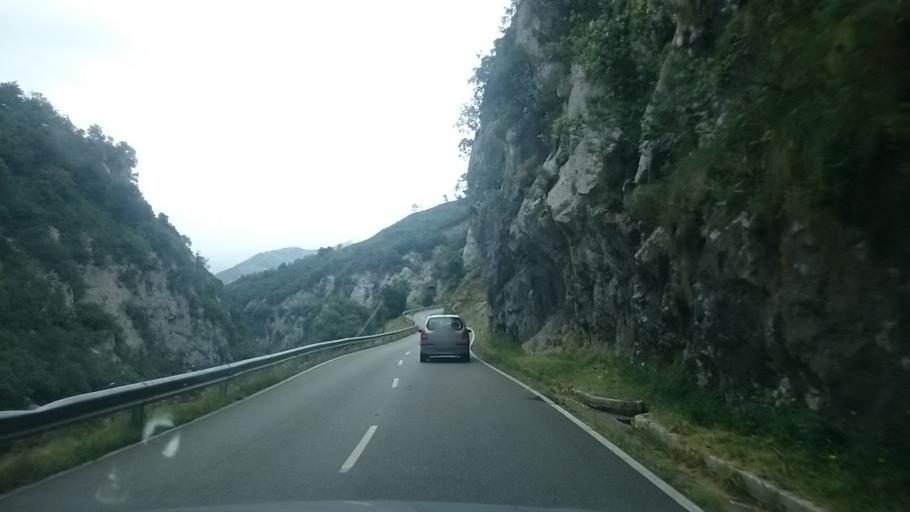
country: ES
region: Asturias
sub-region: Province of Asturias
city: Carrena
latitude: 43.2879
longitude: -4.8301
